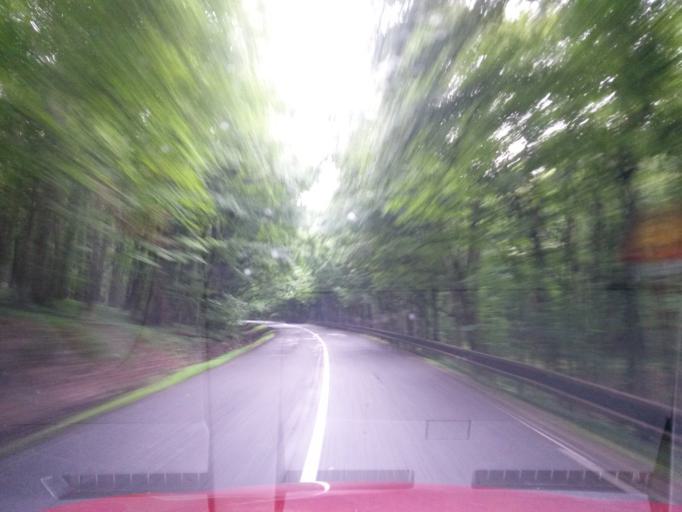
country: SK
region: Banskobystricky
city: Krupina
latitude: 48.1988
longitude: 19.0584
